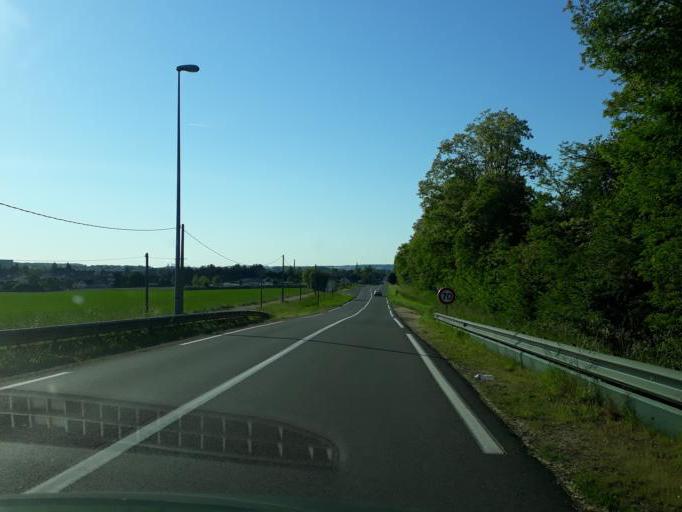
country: FR
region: Centre
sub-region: Departement du Loiret
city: Briare
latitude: 47.6232
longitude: 2.7570
